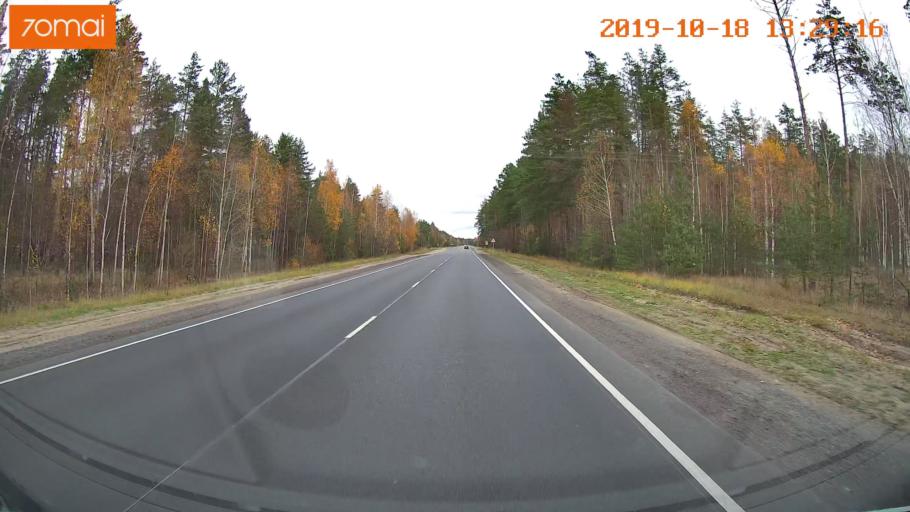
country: RU
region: Rjazan
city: Solotcha
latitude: 54.7918
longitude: 39.8737
